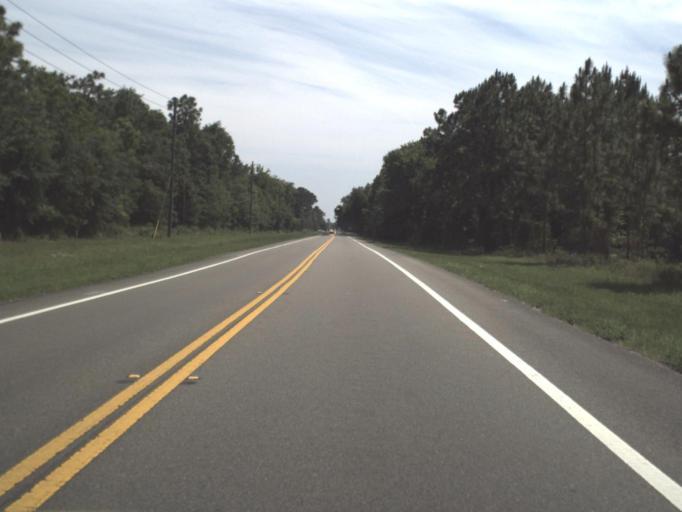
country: US
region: Florida
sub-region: Nassau County
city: Yulee
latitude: 30.5438
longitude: -81.6217
